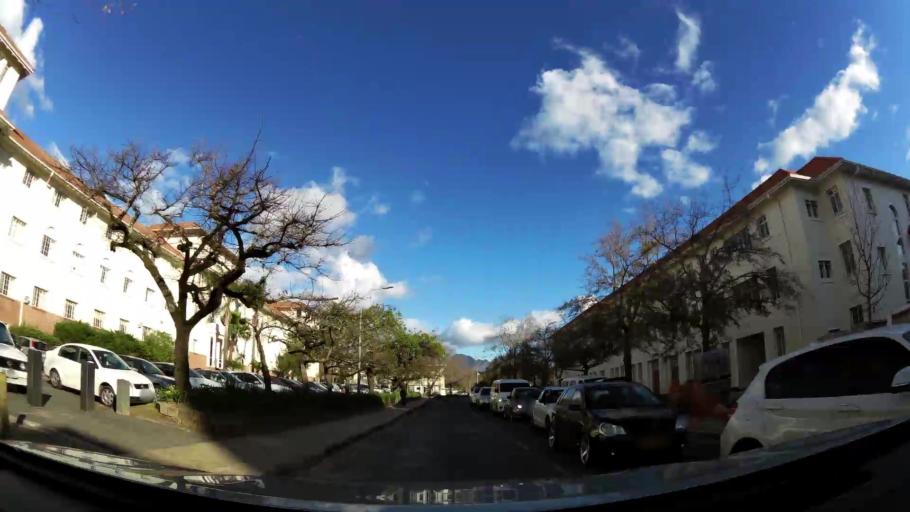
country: ZA
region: Western Cape
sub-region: Cape Winelands District Municipality
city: Stellenbosch
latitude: -33.9327
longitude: 18.8679
